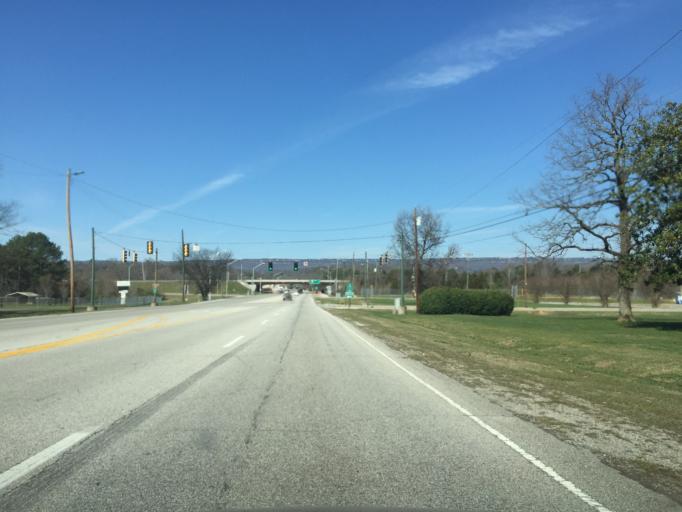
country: US
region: Tennessee
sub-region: Hamilton County
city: East Chattanooga
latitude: 35.1106
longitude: -85.2476
